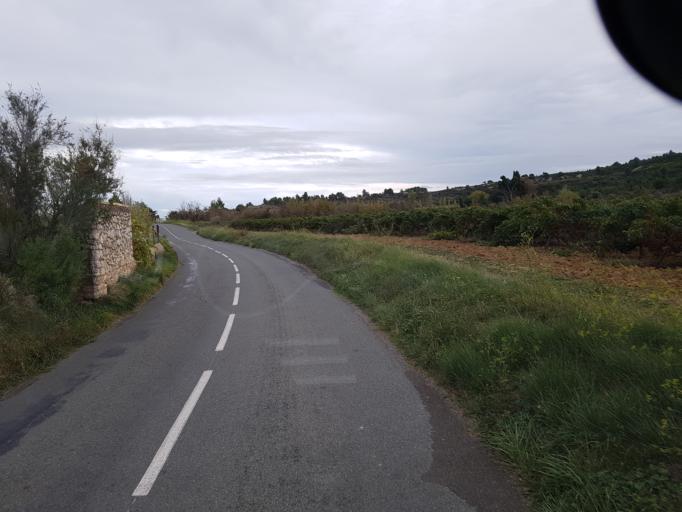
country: FR
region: Languedoc-Roussillon
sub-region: Departement de l'Aude
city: Narbonne
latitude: 43.1371
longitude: 2.9813
